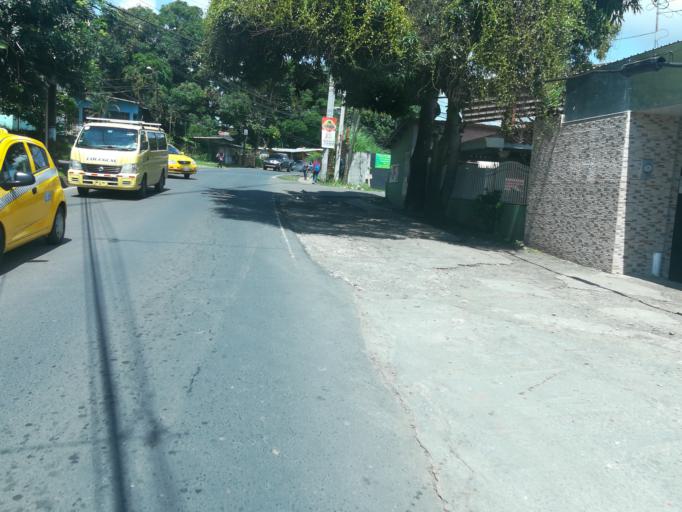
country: PA
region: Panama
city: Tocumen
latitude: 9.0835
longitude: -79.4063
